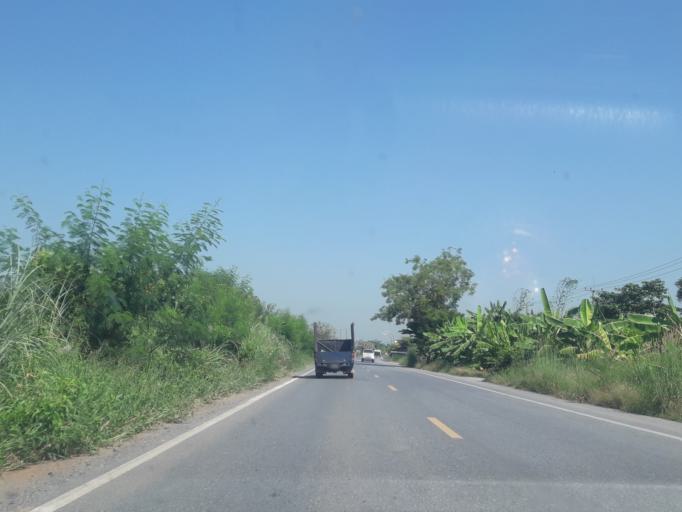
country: TH
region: Sara Buri
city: Nong Khae
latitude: 14.2586
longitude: 100.8233
